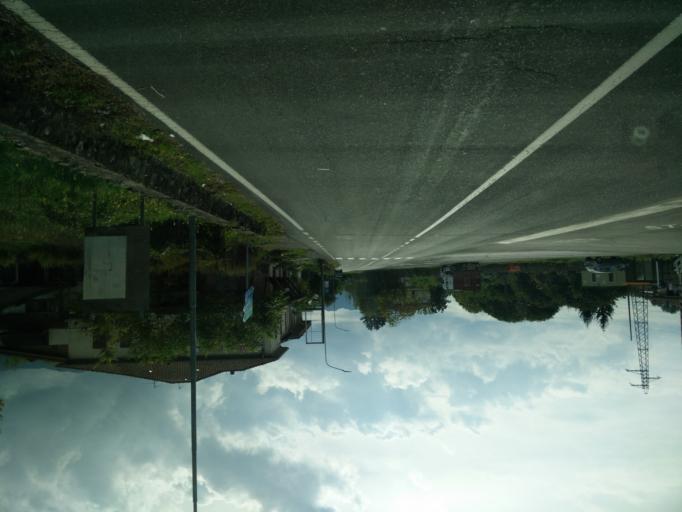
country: IT
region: Tuscany
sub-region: Provincia di Massa-Carrara
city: Filattiera
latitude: 44.3459
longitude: 9.9117
